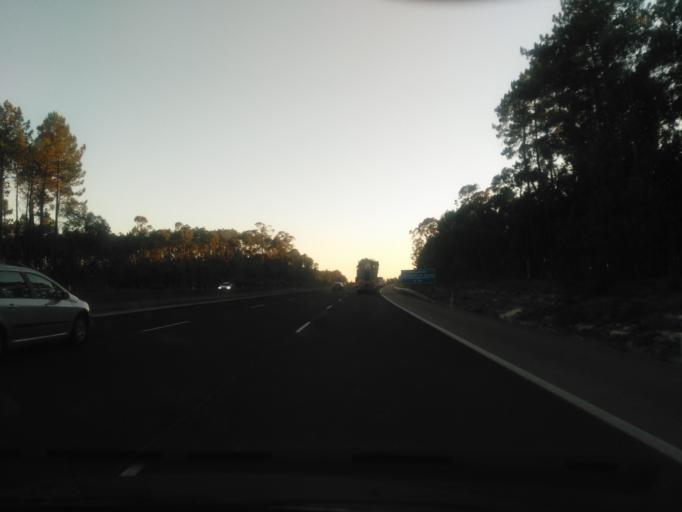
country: PT
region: Leiria
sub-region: Leiria
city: Maceira
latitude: 39.6979
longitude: -8.9249
